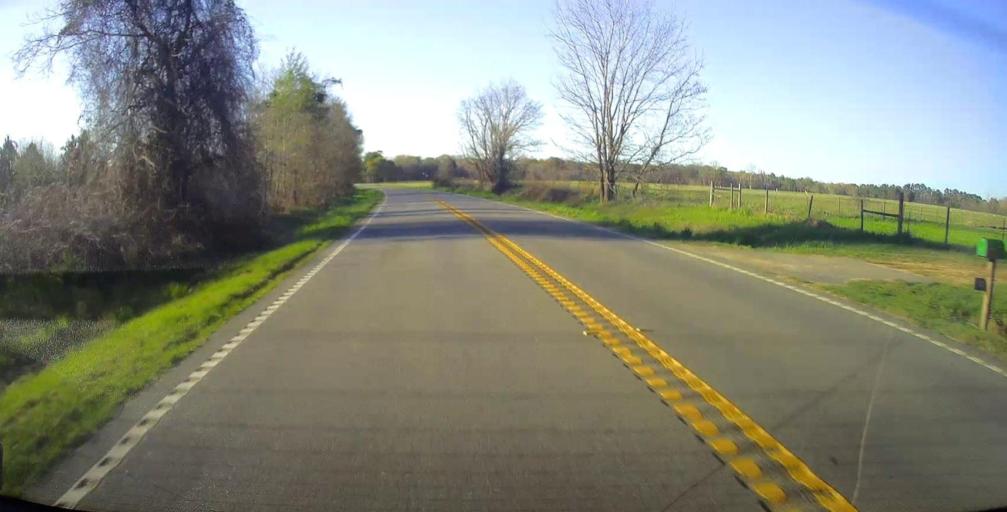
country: US
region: Georgia
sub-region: Pulaski County
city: Hawkinsville
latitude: 32.1870
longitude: -83.3658
